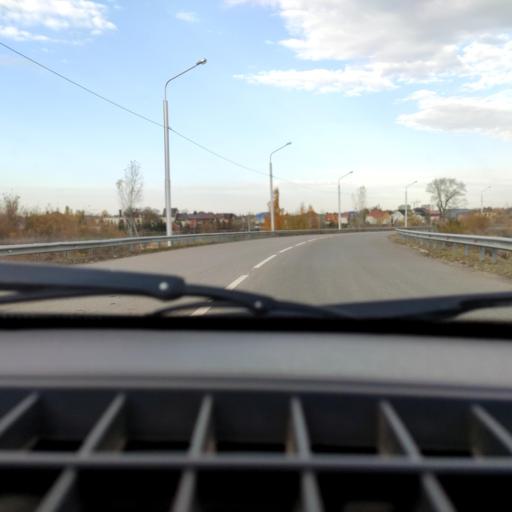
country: RU
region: Bashkortostan
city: Ufa
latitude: 54.7650
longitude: 55.9485
